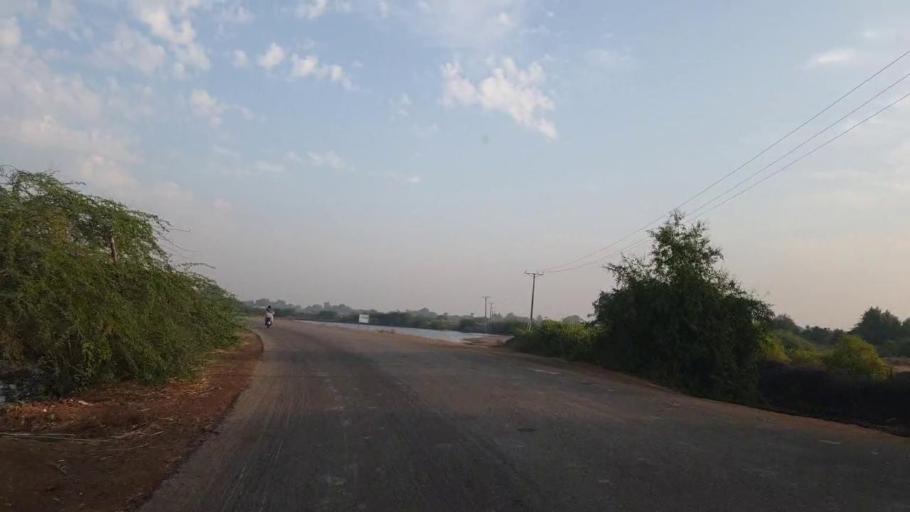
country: PK
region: Sindh
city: Tando Bago
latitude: 24.7121
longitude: 68.9386
